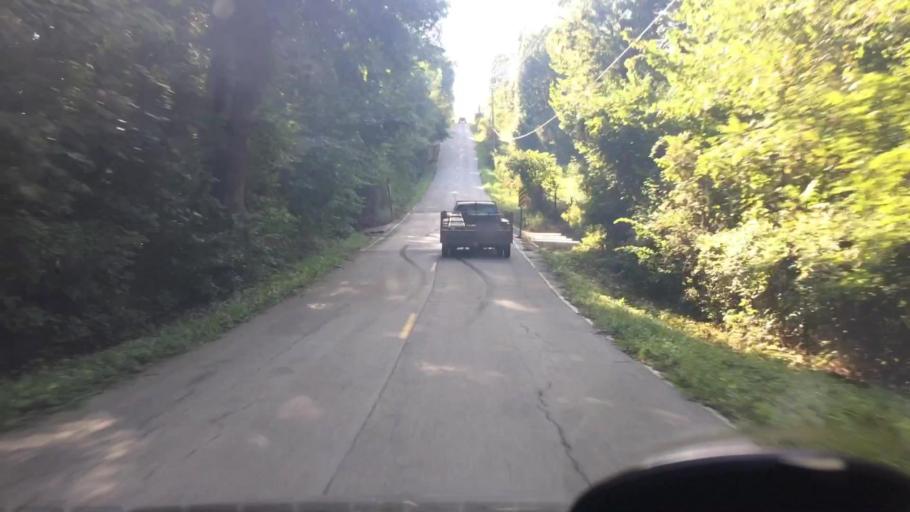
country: US
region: Missouri
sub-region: Greene County
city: Strafford
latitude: 37.2847
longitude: -93.0856
